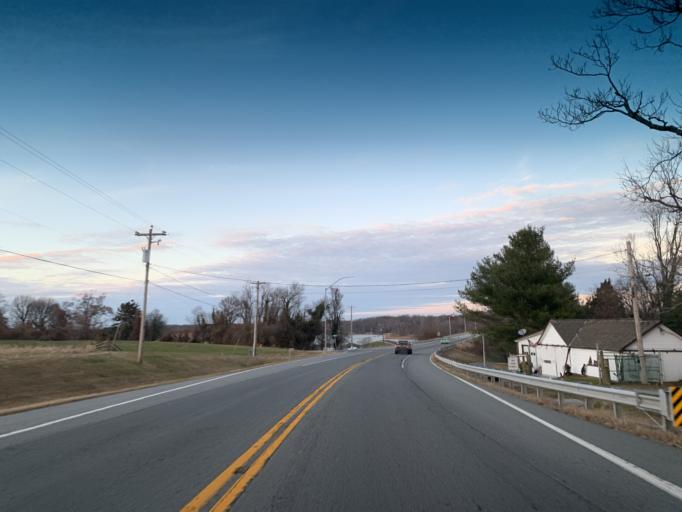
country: US
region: Maryland
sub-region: Cecil County
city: Elkton
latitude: 39.4577
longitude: -75.8714
